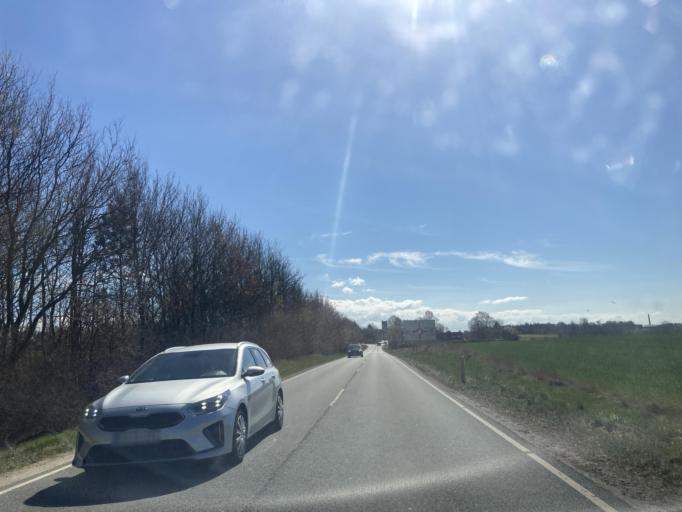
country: DK
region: Capital Region
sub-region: Gribskov Kommune
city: Graested
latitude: 56.0311
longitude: 12.2809
